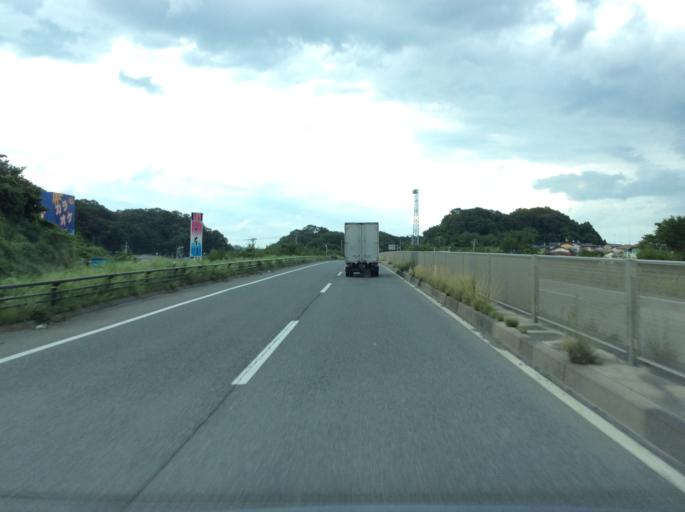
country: JP
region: Fukushima
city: Iwaki
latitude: 37.0252
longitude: 140.8959
